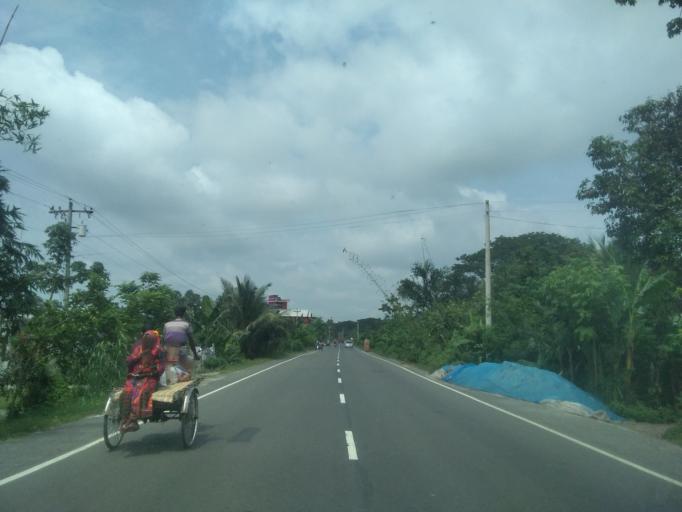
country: BD
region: Khulna
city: Kesabpur
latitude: 22.8206
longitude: 89.2656
